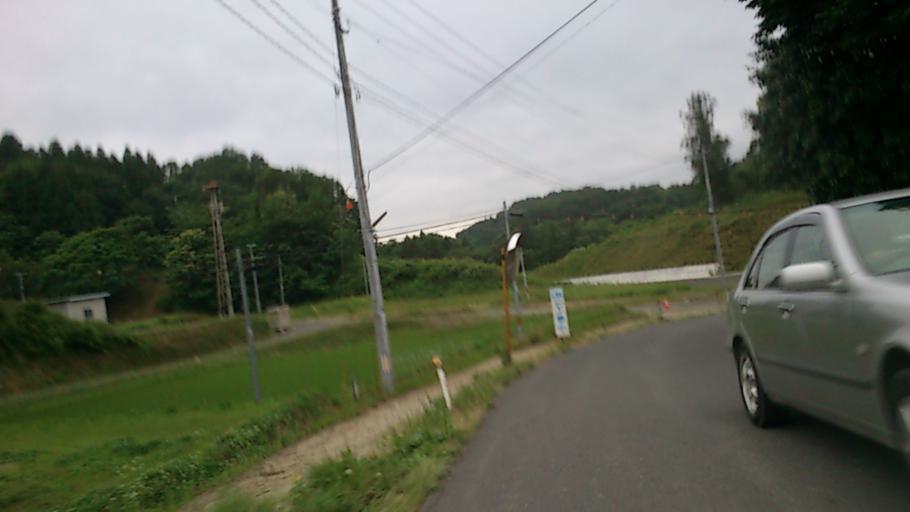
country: JP
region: Fukushima
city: Fukushima-shi
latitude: 37.6642
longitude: 140.5065
